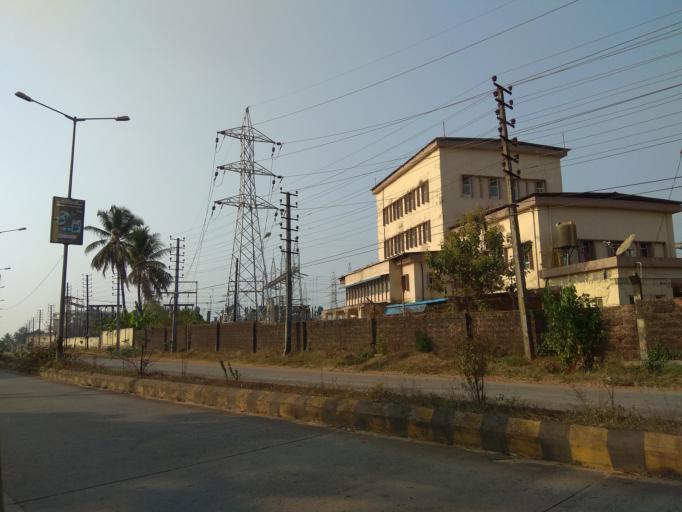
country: IN
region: Karnataka
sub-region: Dakshina Kannada
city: Mangalore
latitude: 12.9247
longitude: 74.8610
